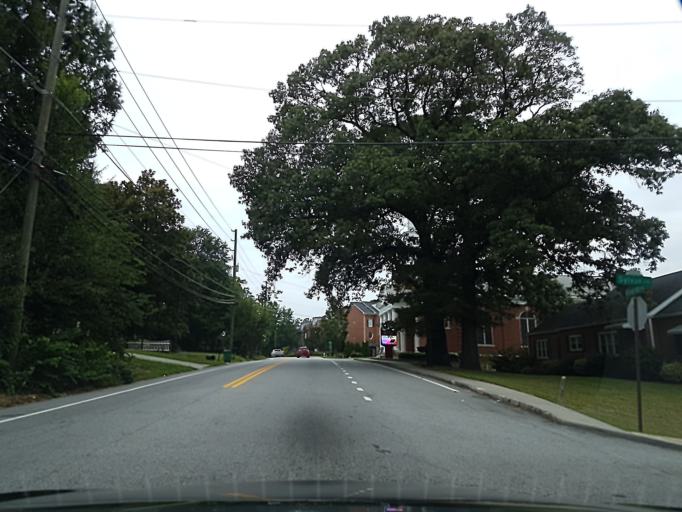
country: US
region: Georgia
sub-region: DeKalb County
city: North Atlanta
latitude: 33.8548
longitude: -84.3393
